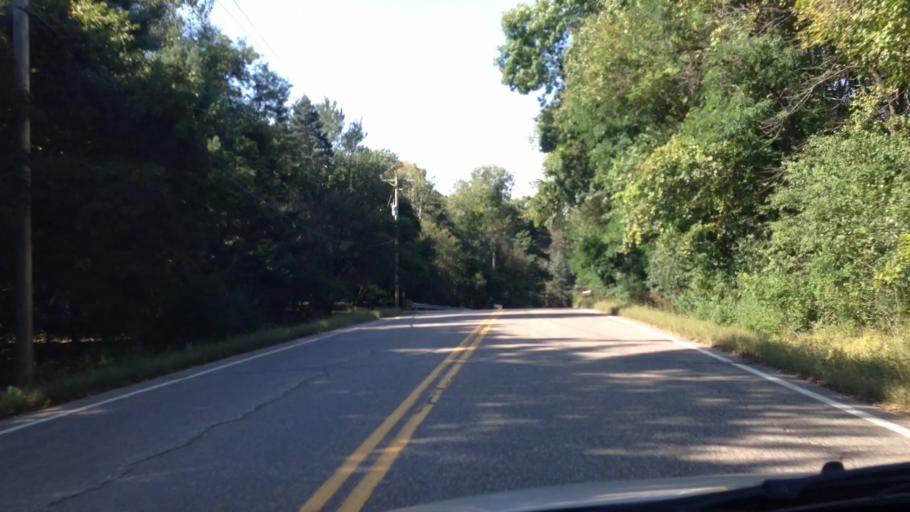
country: US
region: Minnesota
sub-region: Washington County
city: Stillwater
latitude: 45.0820
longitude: -92.8118
